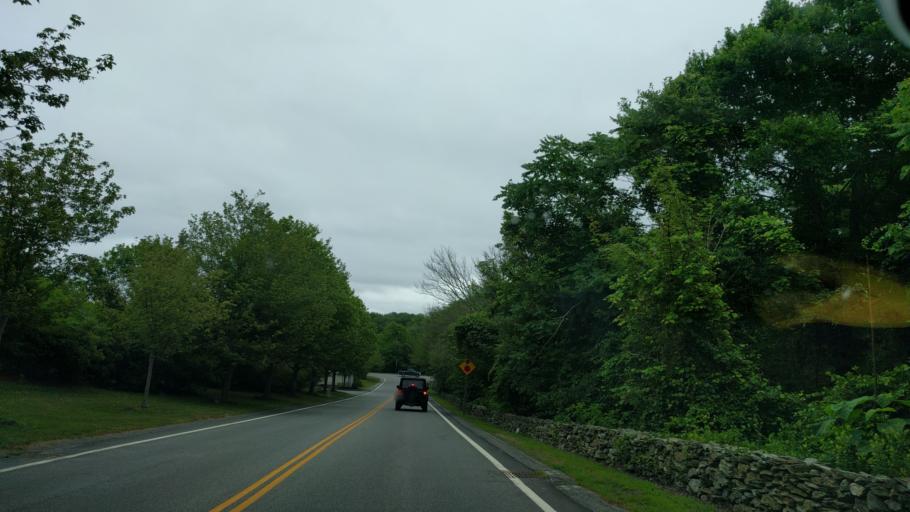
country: US
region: Rhode Island
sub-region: Newport County
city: Jamestown
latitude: 41.5258
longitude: -71.3770
